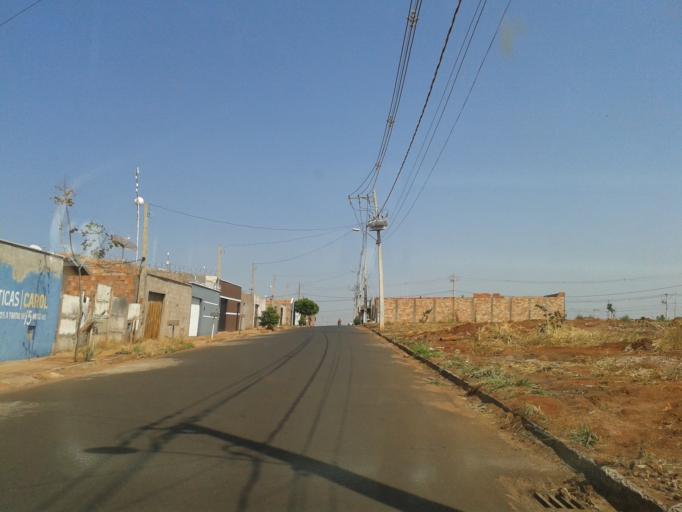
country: BR
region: Minas Gerais
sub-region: Ituiutaba
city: Ituiutaba
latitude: -19.0157
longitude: -49.4566
